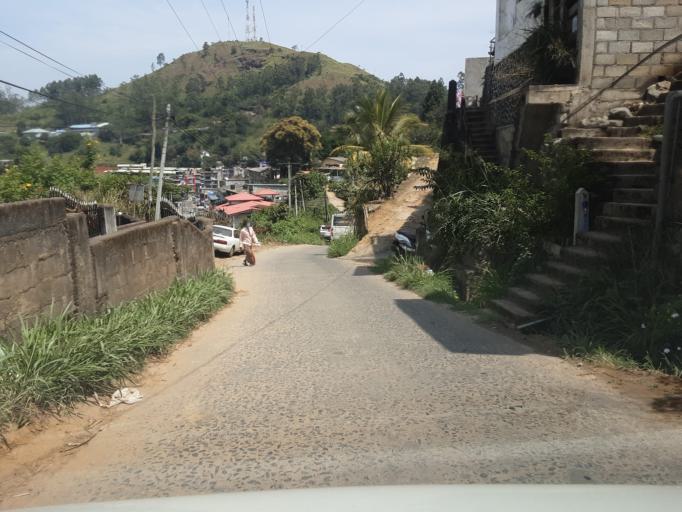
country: LK
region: Central
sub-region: Nuwara Eliya District
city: Nuwara Eliya
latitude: 6.9030
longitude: 80.9094
